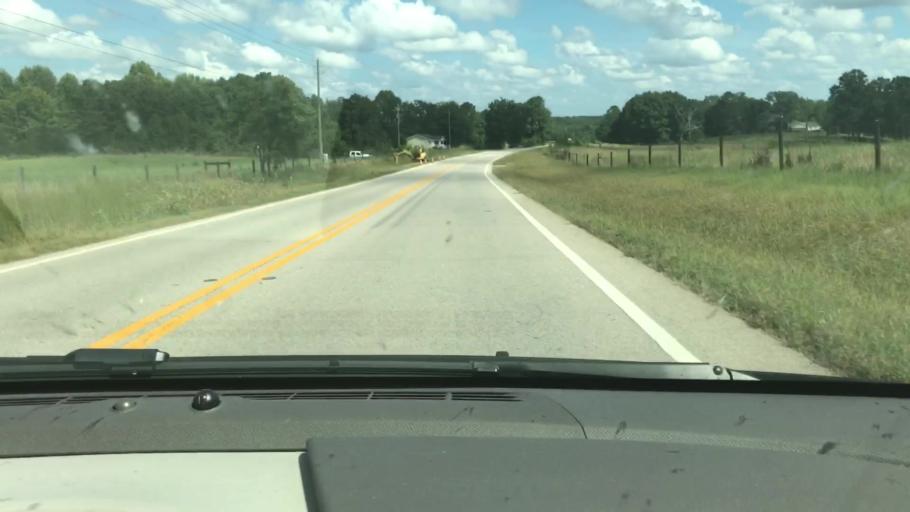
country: US
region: Georgia
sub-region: Troup County
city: West Point
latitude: 32.8851
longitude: -85.0336
